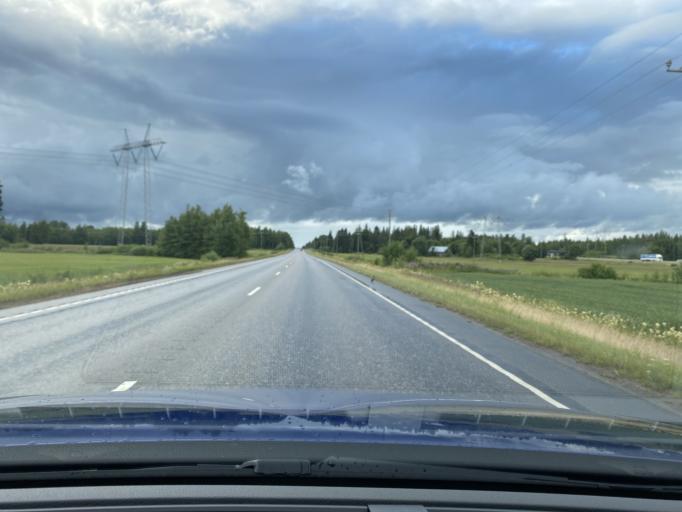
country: FI
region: Uusimaa
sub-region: Helsinki
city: Nurmijaervi
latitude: 60.5365
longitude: 24.8376
